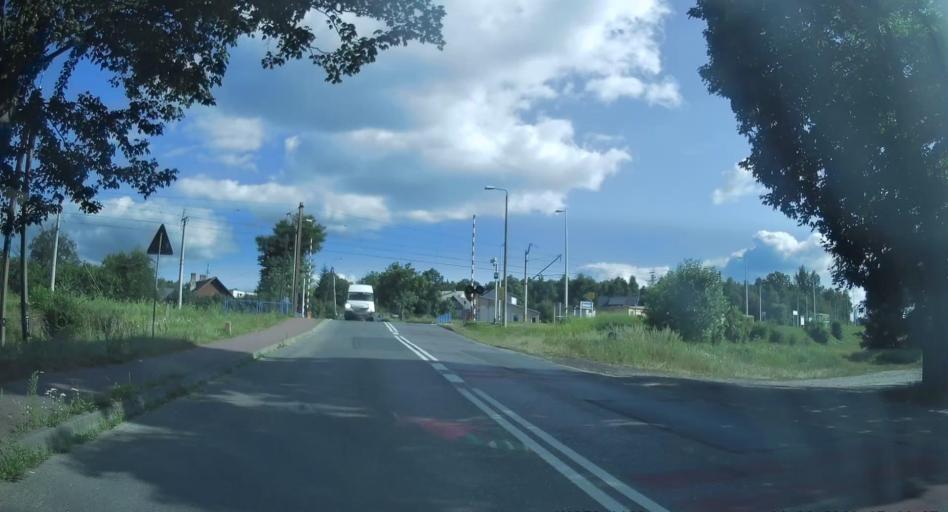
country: PL
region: Swietokrzyskie
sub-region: Powiat skarzyski
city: Suchedniow
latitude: 51.0247
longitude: 20.8367
